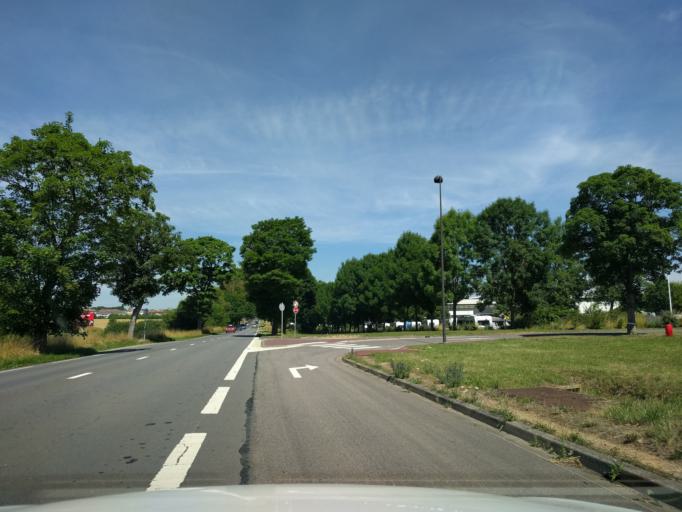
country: FR
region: Lorraine
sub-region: Departement de la Moselle
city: Peltre
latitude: 49.0975
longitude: 6.2183
